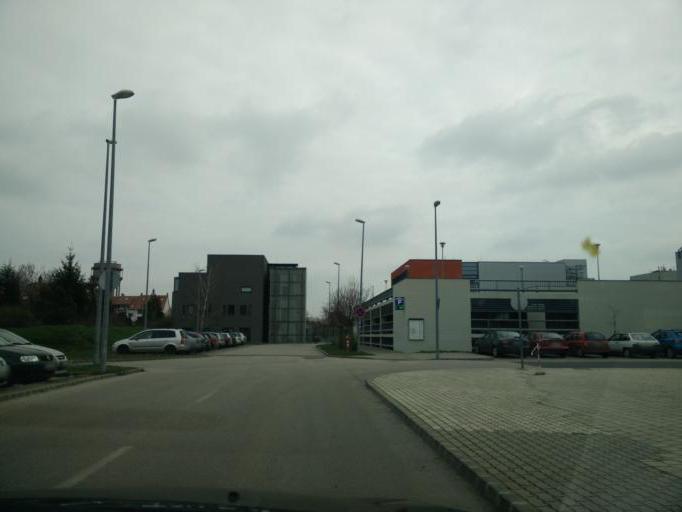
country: HU
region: Gyor-Moson-Sopron
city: Gyor
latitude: 47.6954
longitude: 17.6265
